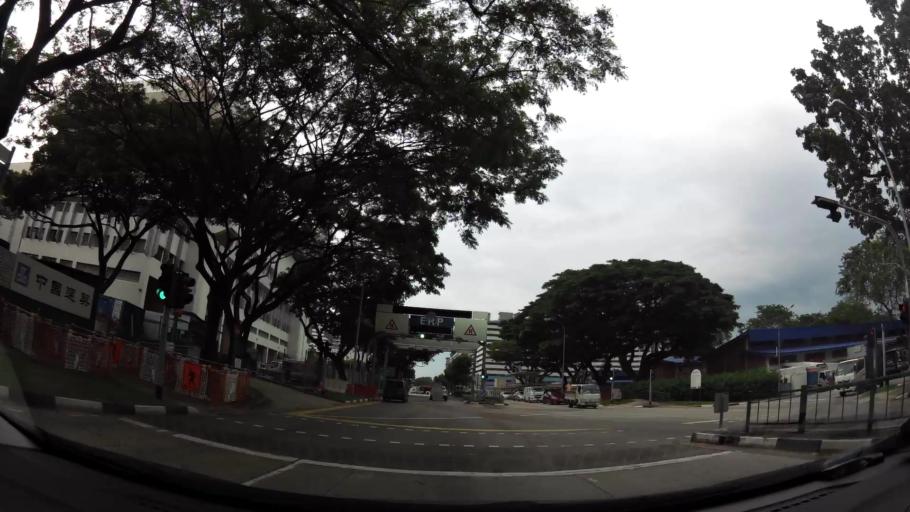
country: SG
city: Singapore
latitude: 1.3199
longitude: 103.8719
